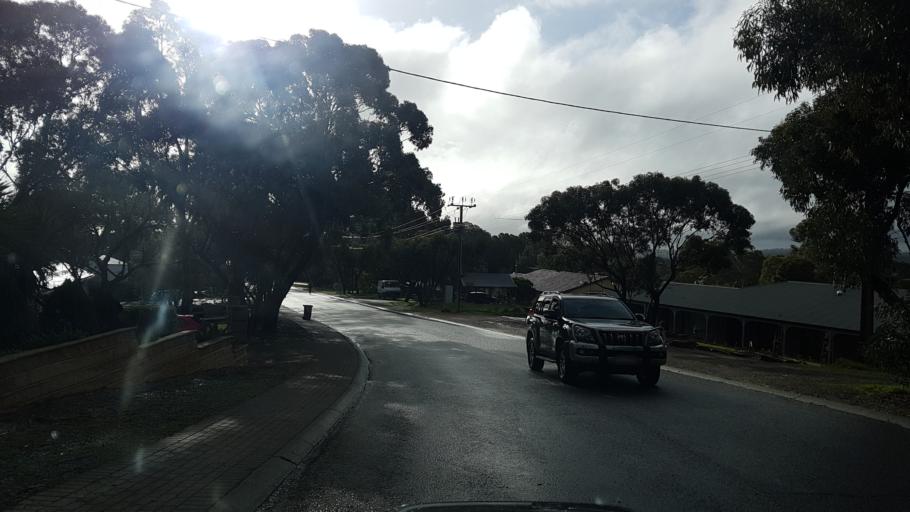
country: AU
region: South Australia
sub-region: Onkaparinga
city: Craigburn Farm
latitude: -35.0676
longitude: 138.6120
